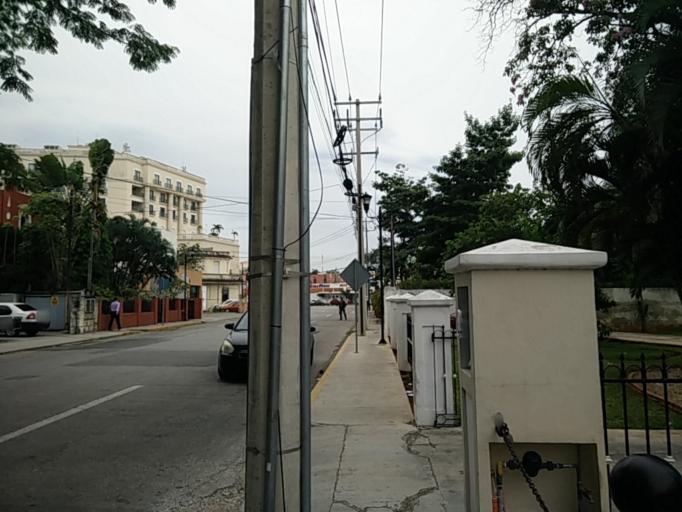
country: MX
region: Yucatan
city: Merida
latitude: 20.9880
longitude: -89.6188
